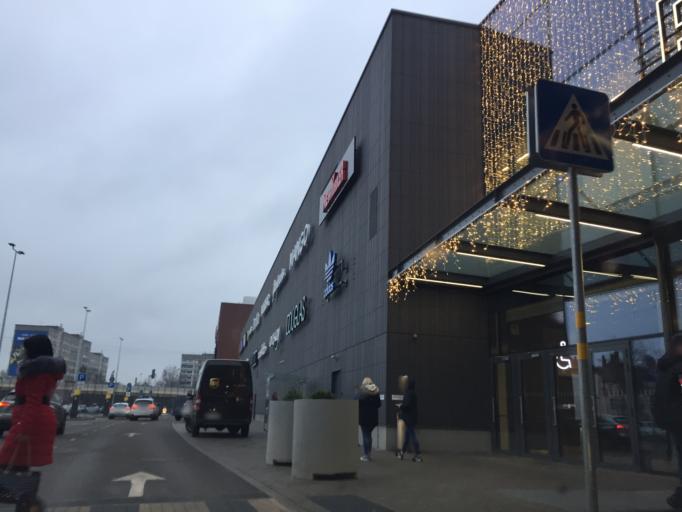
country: LV
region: Riga
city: Riga
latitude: 56.9235
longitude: 24.1740
